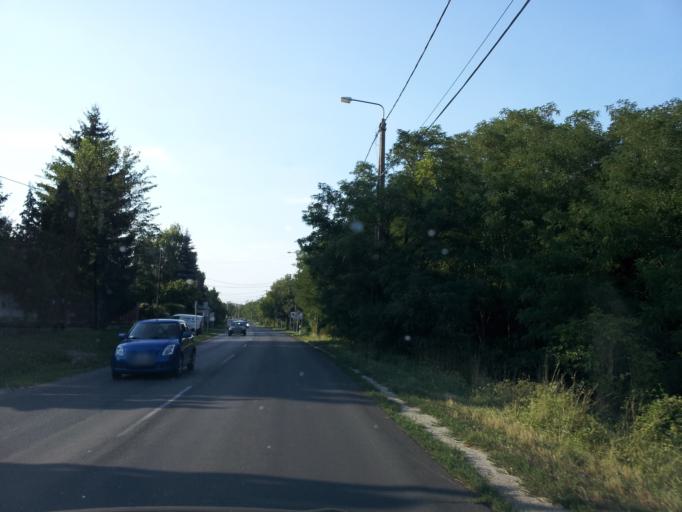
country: HU
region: Pest
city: Tahitotfalu
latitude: 47.7383
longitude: 19.0876
